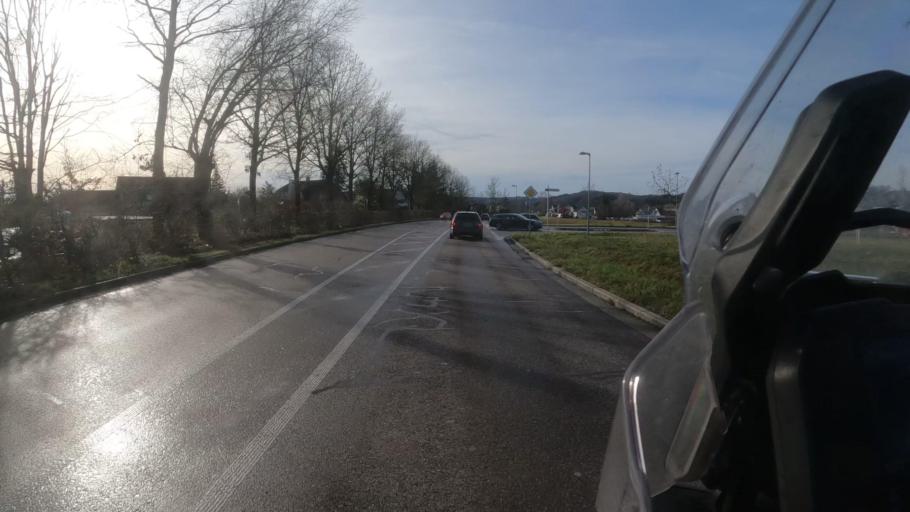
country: DE
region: Baden-Wuerttemberg
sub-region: Freiburg Region
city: Jestetten
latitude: 47.6567
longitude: 8.5809
